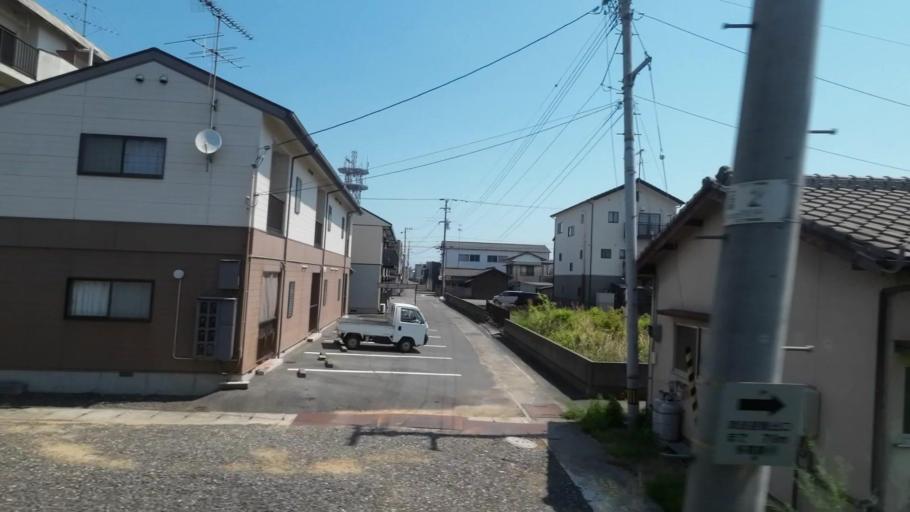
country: JP
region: Ehime
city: Saijo
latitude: 33.9332
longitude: 133.0825
